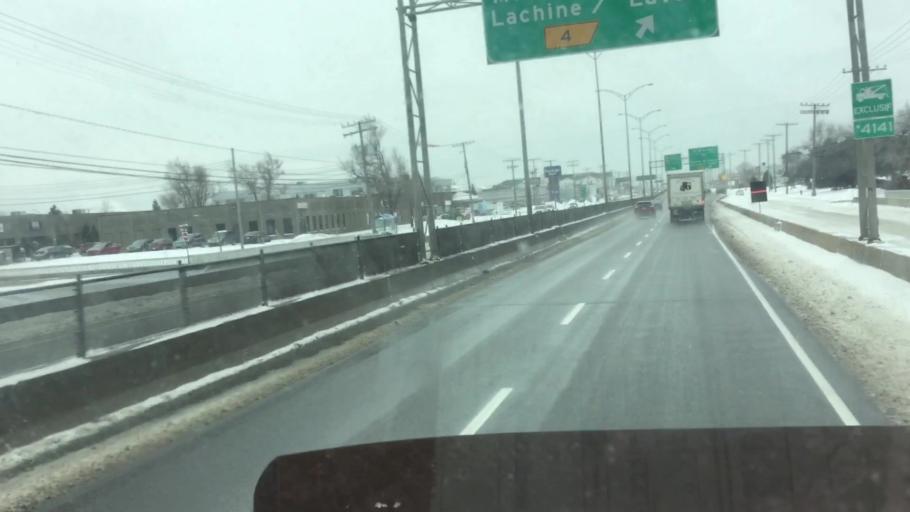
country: CA
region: Quebec
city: Hampstead
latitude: 45.4820
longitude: -73.6968
